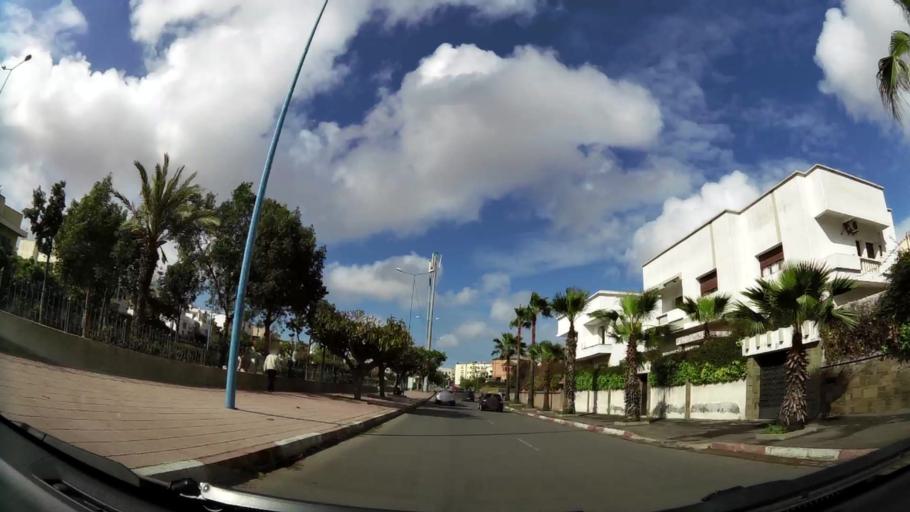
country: MA
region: Grand Casablanca
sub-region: Casablanca
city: Casablanca
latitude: 33.5483
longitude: -7.6040
